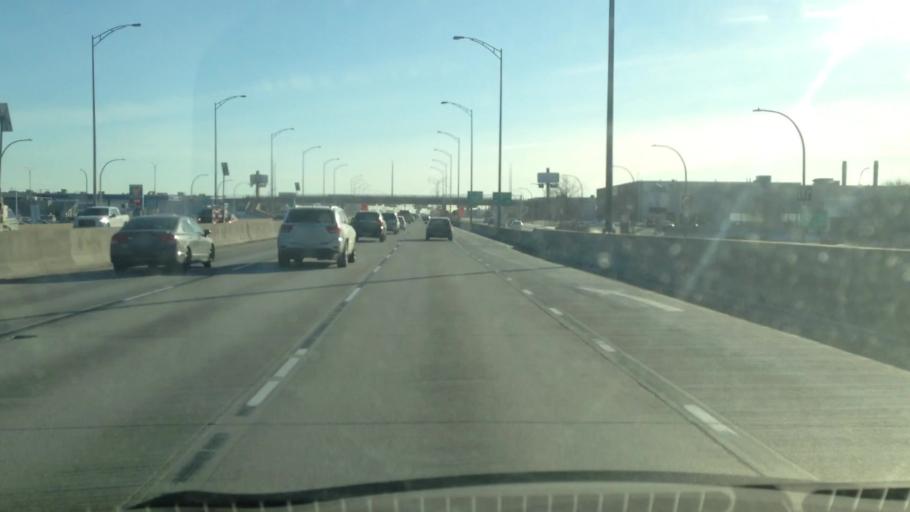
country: CA
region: Quebec
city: Dorval
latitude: 45.5005
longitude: -73.7530
